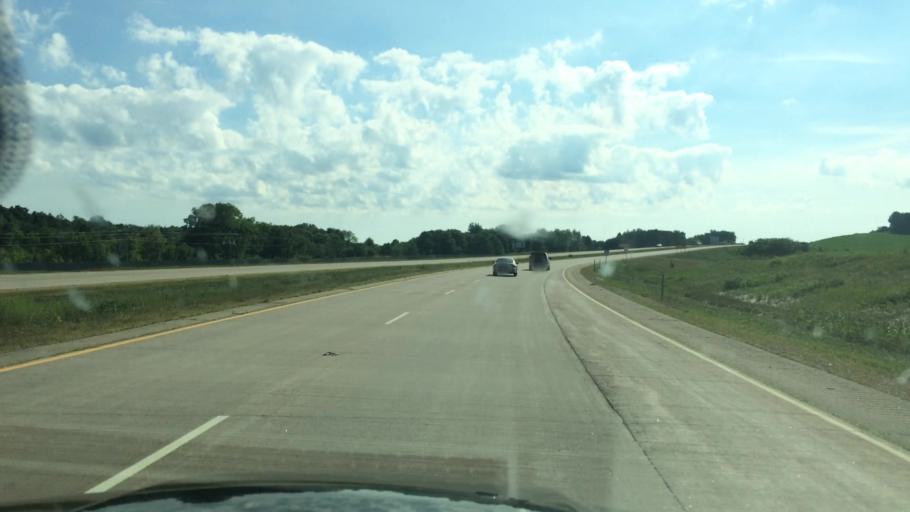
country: US
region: Wisconsin
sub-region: Shawano County
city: Wittenberg
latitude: 44.8253
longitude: -89.1151
